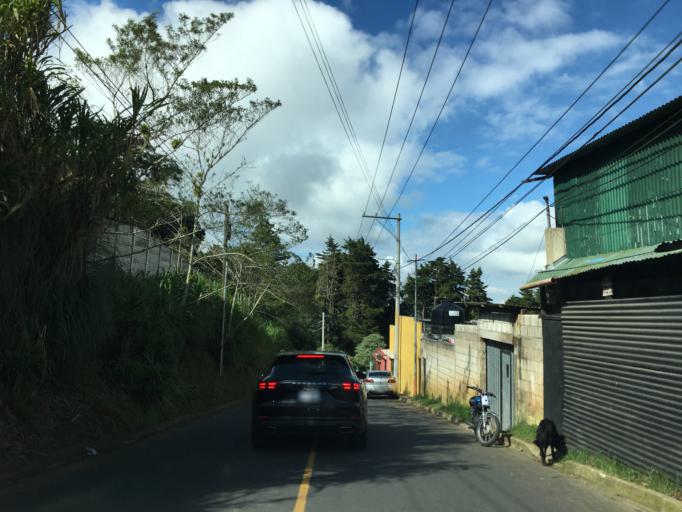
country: GT
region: Guatemala
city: San Jose Pinula
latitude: 14.5693
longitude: -90.4401
